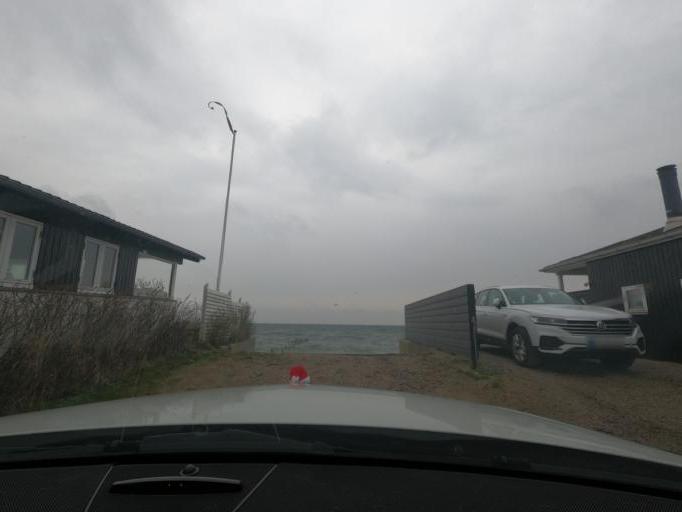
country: DK
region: South Denmark
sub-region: Haderslev Kommune
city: Starup
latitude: 55.1920
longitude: 9.5839
